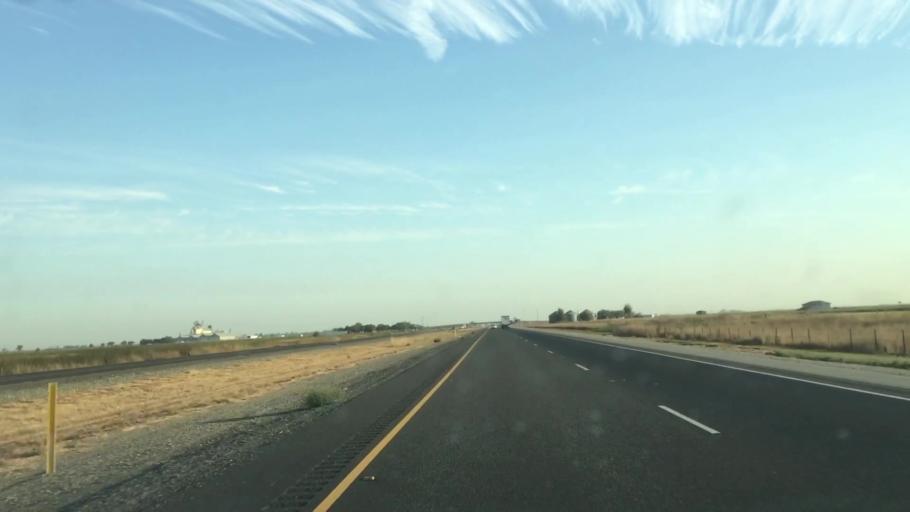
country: US
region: California
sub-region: Colusa County
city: Maxwell
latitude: 39.2300
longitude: -122.1820
